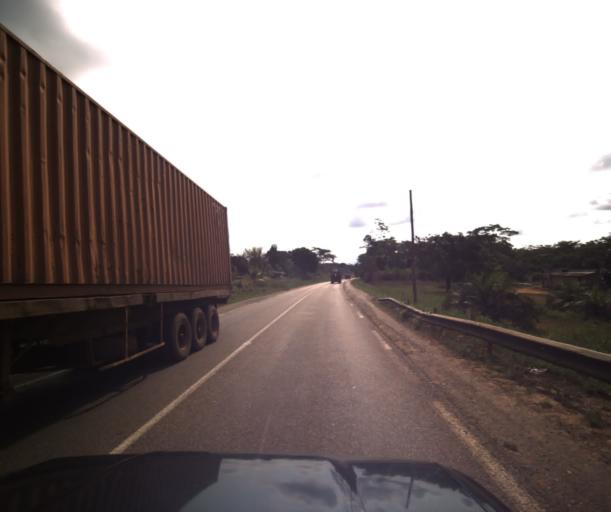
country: CM
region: Littoral
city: Edea
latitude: 3.9503
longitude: 10.0277
